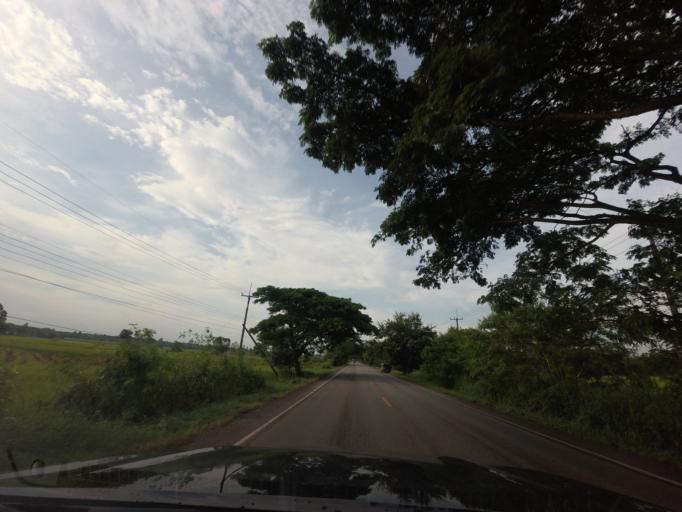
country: TH
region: Changwat Udon Thani
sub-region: Amphoe Ban Phue
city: Ban Phue
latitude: 17.7584
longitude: 102.3977
